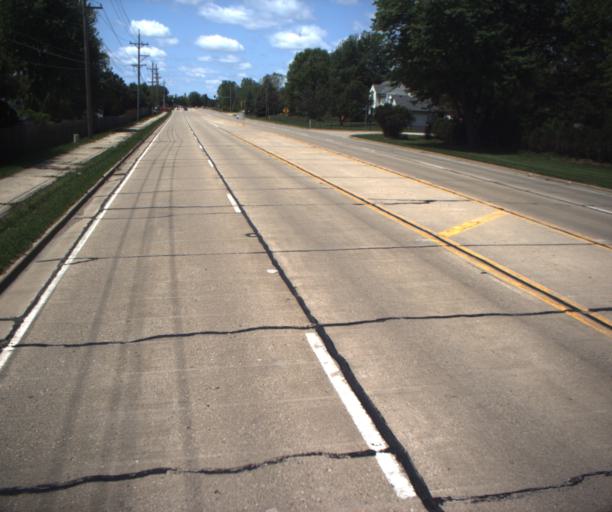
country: US
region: Illinois
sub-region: Kane County
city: Batavia
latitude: 41.8639
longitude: -88.3249
